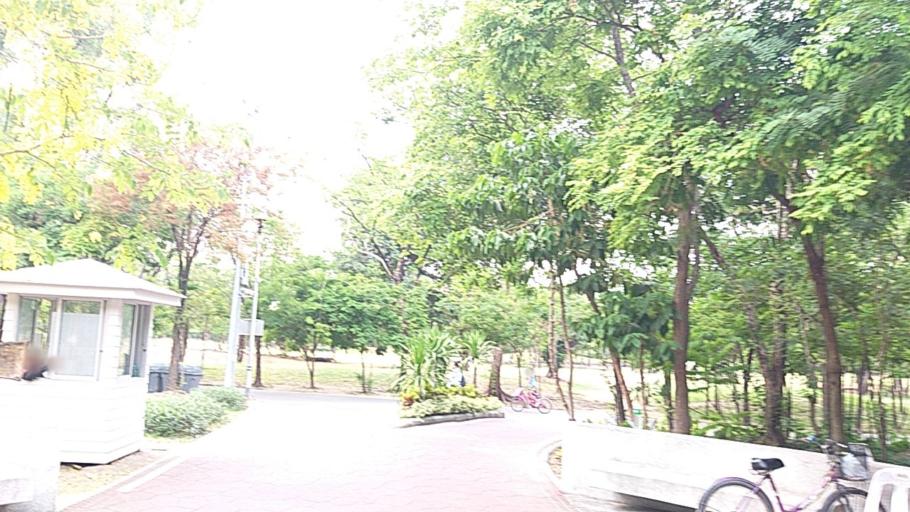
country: TH
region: Bangkok
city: Bang Sue
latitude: 13.8081
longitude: 100.5532
